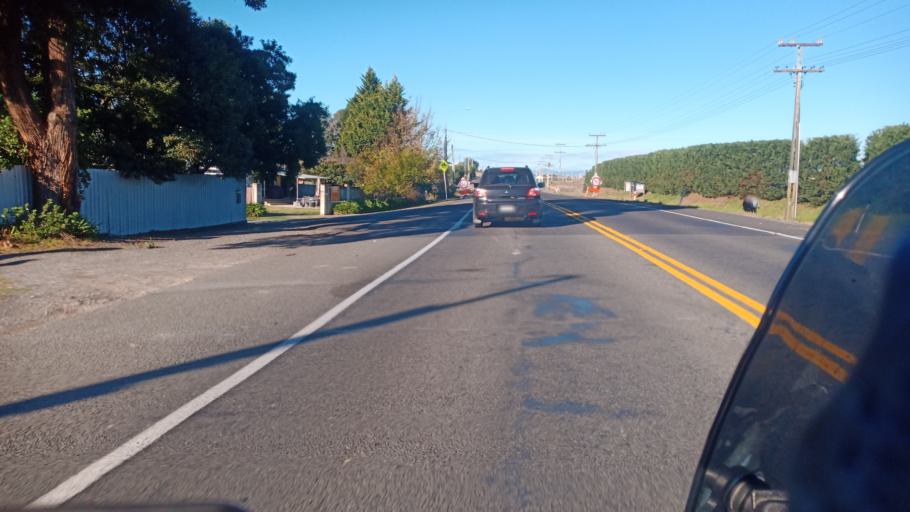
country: NZ
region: Hawke's Bay
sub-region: Napier City
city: Napier
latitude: -39.4382
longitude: 176.8702
